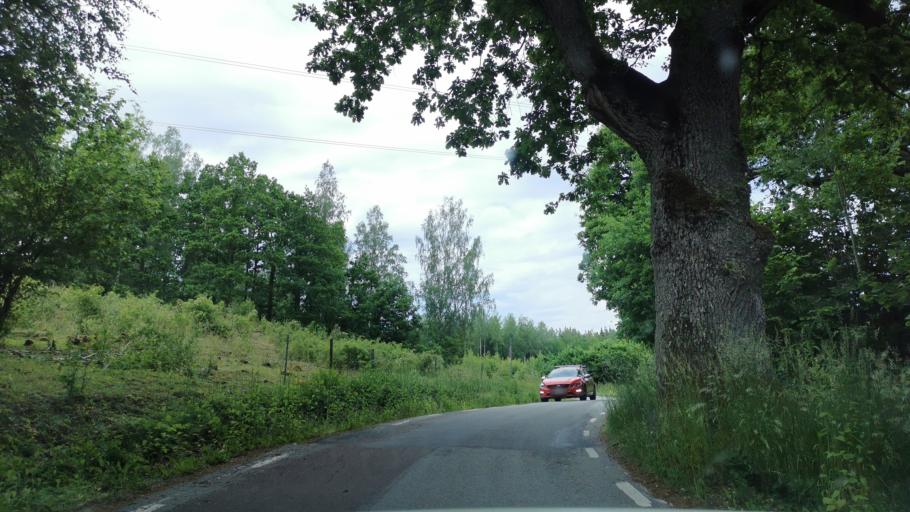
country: SE
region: Vaestra Goetaland
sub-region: Bengtsfors Kommun
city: Dals Langed
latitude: 58.8469
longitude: 12.4078
